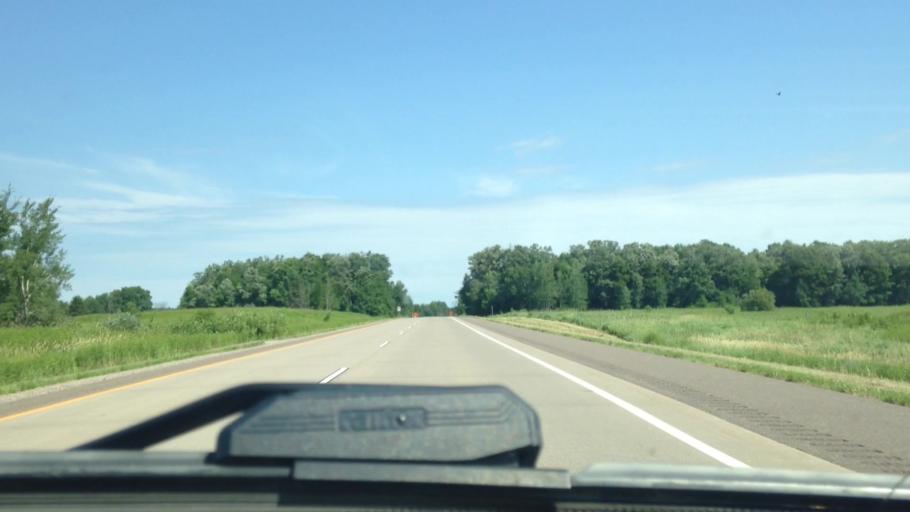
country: US
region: Wisconsin
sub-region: Barron County
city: Rice Lake
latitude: 45.5499
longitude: -91.7637
